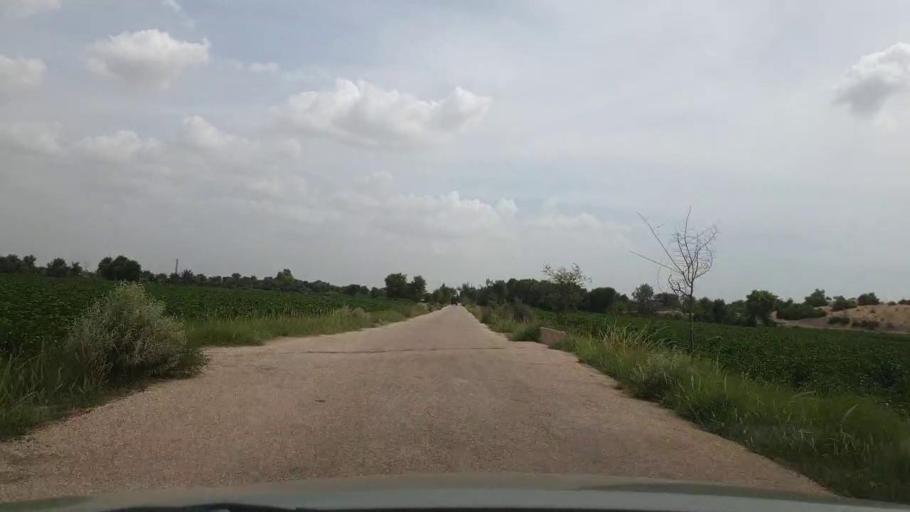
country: PK
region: Sindh
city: Kot Diji
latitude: 27.1594
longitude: 69.0351
